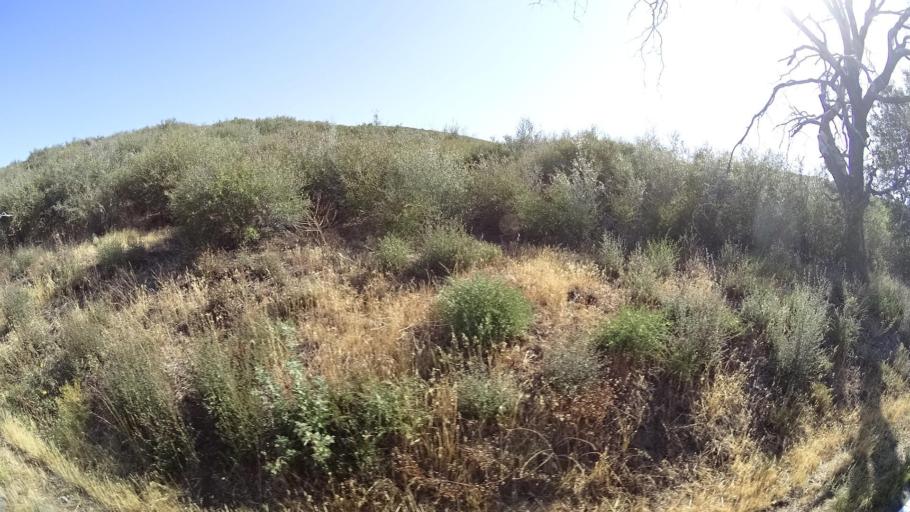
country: US
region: California
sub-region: San Diego County
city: Pine Valley
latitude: 32.9086
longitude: -116.4593
